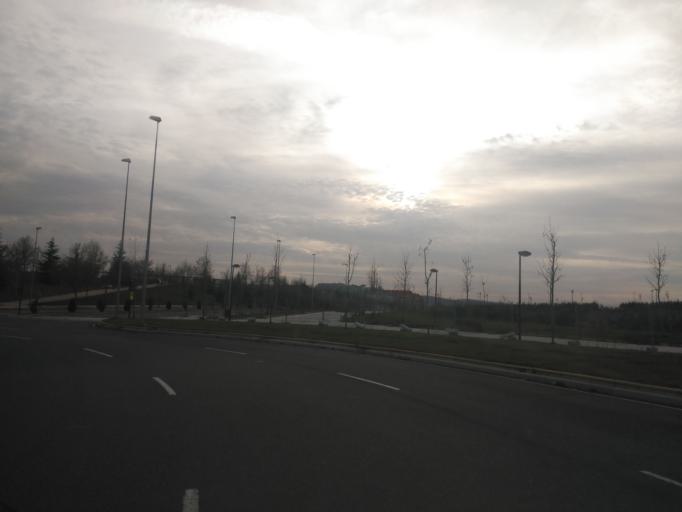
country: ES
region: Castille and Leon
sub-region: Provincia de Salamanca
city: Salamanca
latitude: 40.9679
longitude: -5.6872
